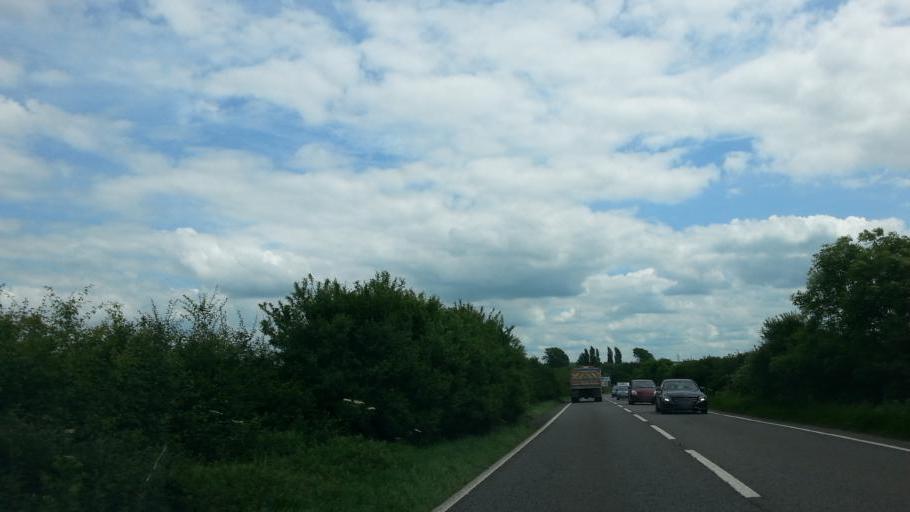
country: GB
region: England
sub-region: Lincolnshire
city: Barrowby
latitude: 52.9312
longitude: -0.7383
